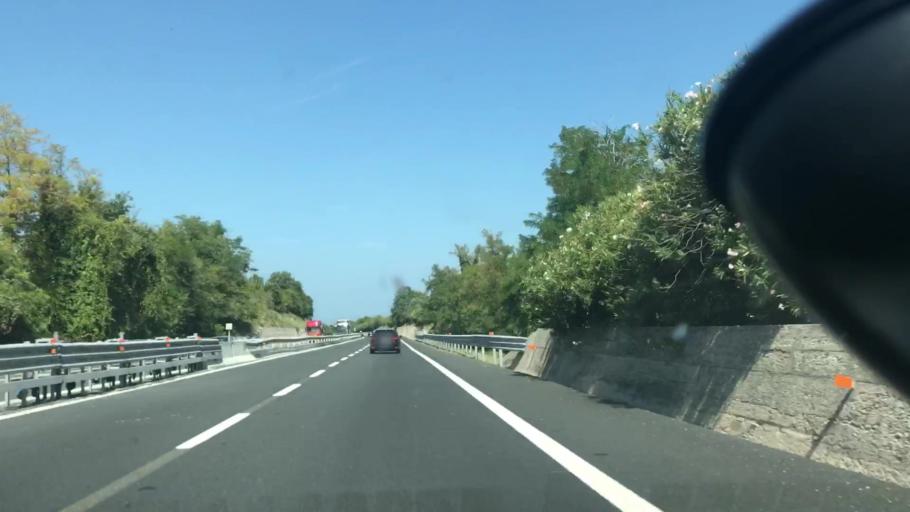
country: IT
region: Abruzzo
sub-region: Provincia di Chieti
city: Ortona
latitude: 42.3425
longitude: 14.3581
